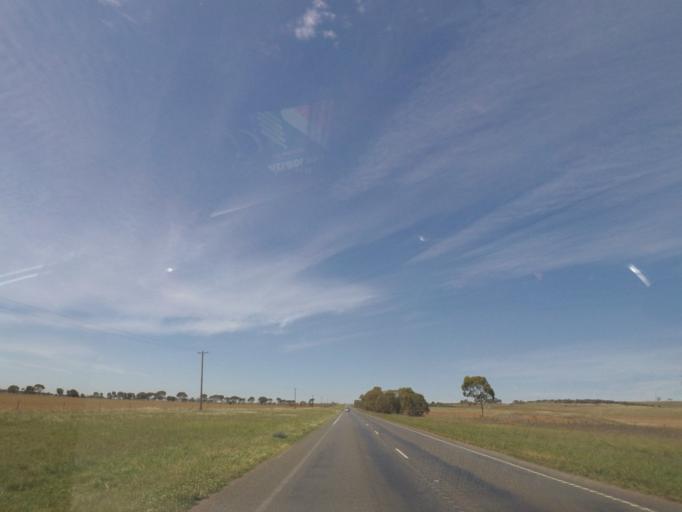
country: AU
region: Victoria
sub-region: Moorabool
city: Bacchus Marsh
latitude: -37.7634
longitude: 144.4405
